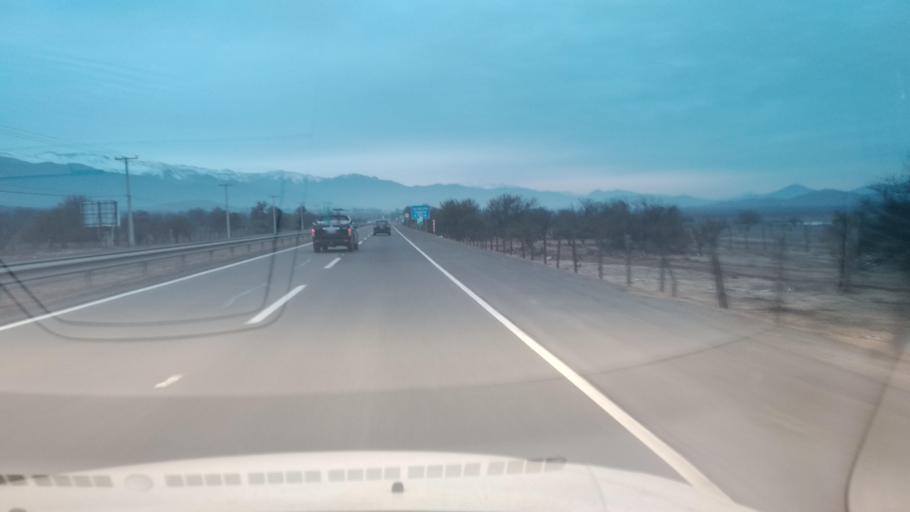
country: CL
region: Santiago Metropolitan
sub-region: Provincia de Chacabuco
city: Chicureo Abajo
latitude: -33.1195
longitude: -70.6798
